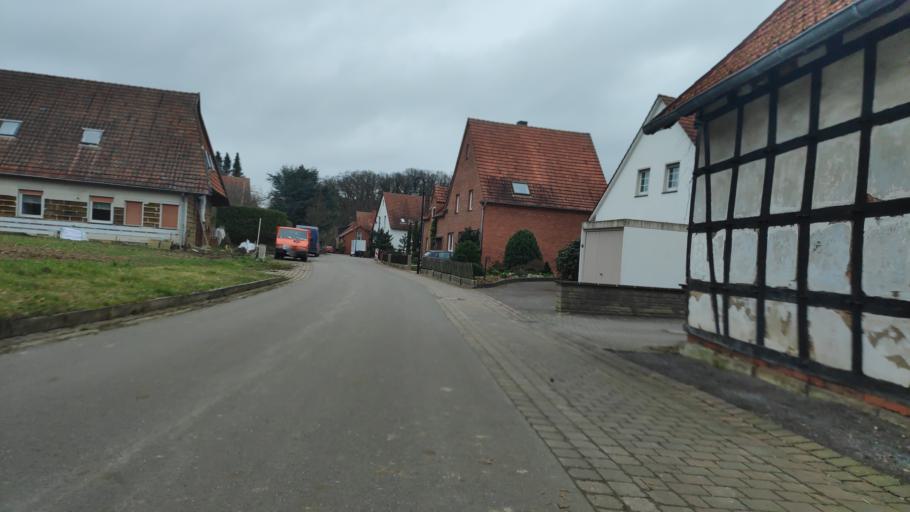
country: DE
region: North Rhine-Westphalia
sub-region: Regierungsbezirk Detmold
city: Hille
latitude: 52.3085
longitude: 8.8234
